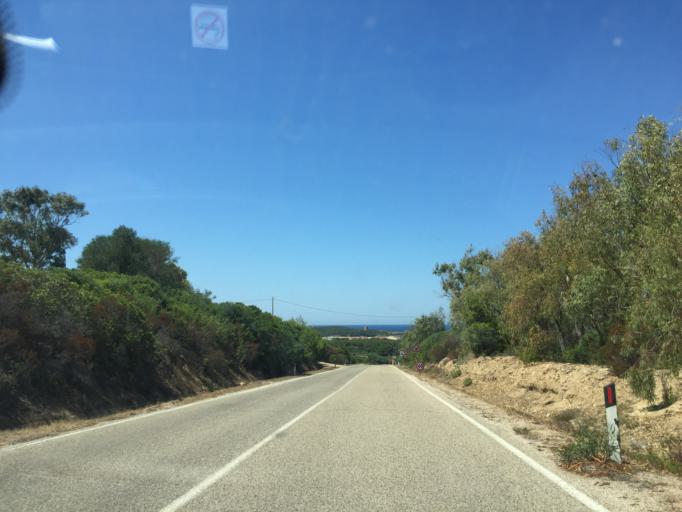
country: IT
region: Sardinia
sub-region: Provincia di Olbia-Tempio
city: Aglientu
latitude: 41.1195
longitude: 9.0723
